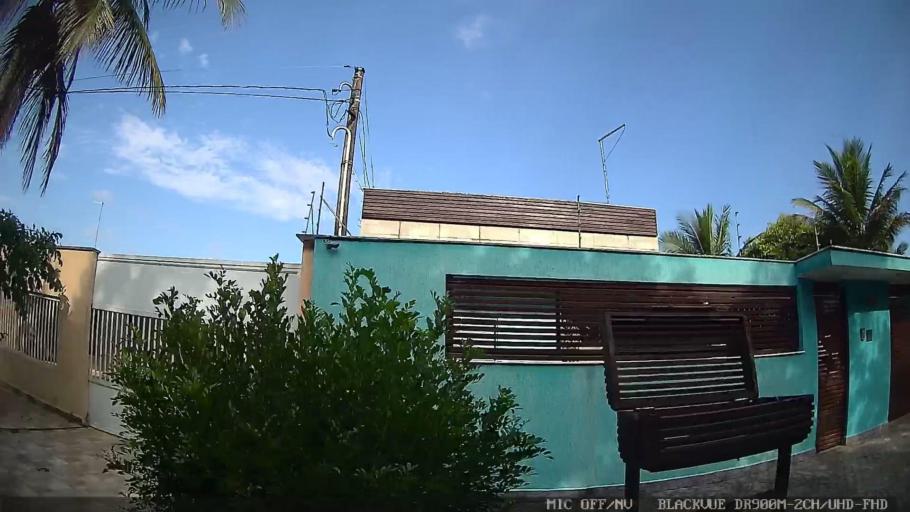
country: BR
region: Sao Paulo
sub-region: Caraguatatuba
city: Caraguatatuba
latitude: -23.6541
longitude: -45.4320
